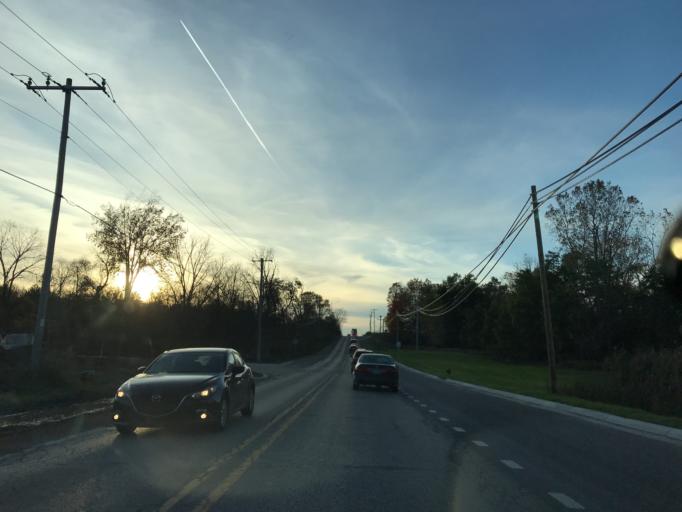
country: US
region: Michigan
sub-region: Oakland County
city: Novi
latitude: 42.4950
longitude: -83.4966
